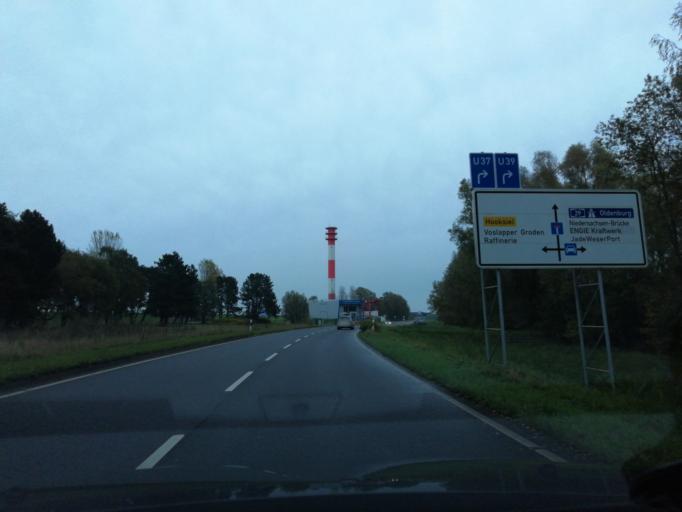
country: DE
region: Lower Saxony
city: Wilhelmshaven
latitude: 53.5816
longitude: 8.1263
